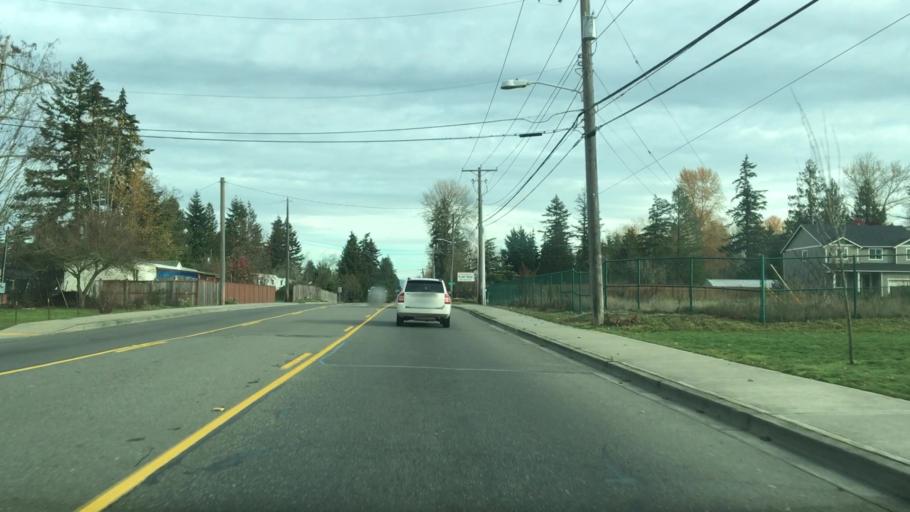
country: US
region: Washington
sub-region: Pierce County
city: Frederickson
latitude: 47.1111
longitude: -122.3230
